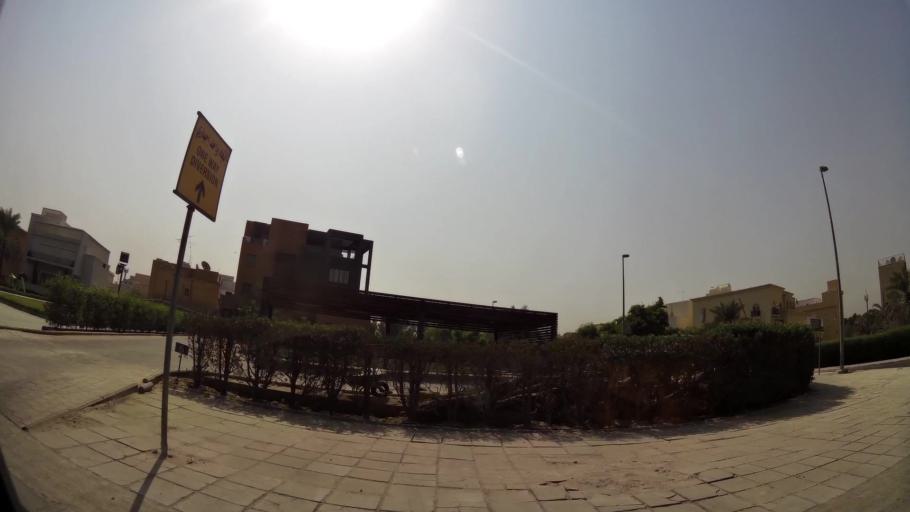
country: KW
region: Al Asimah
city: Ash Shamiyah
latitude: 29.3452
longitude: 47.9607
